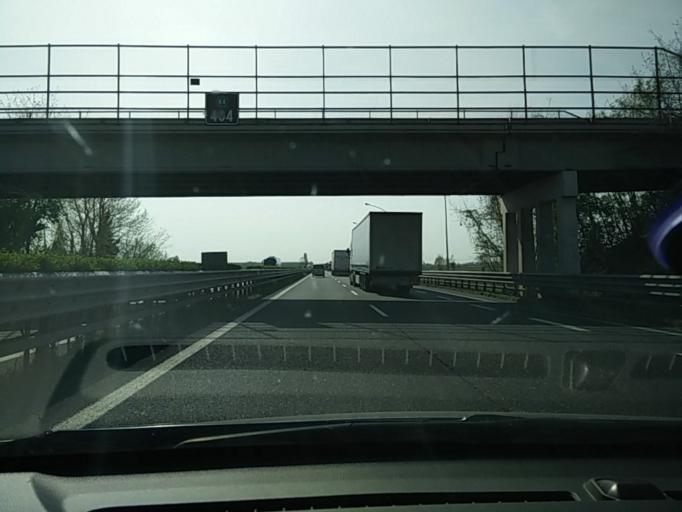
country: IT
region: Veneto
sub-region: Provincia di Venezia
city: Teglio Veneto
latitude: 45.8037
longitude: 12.8780
